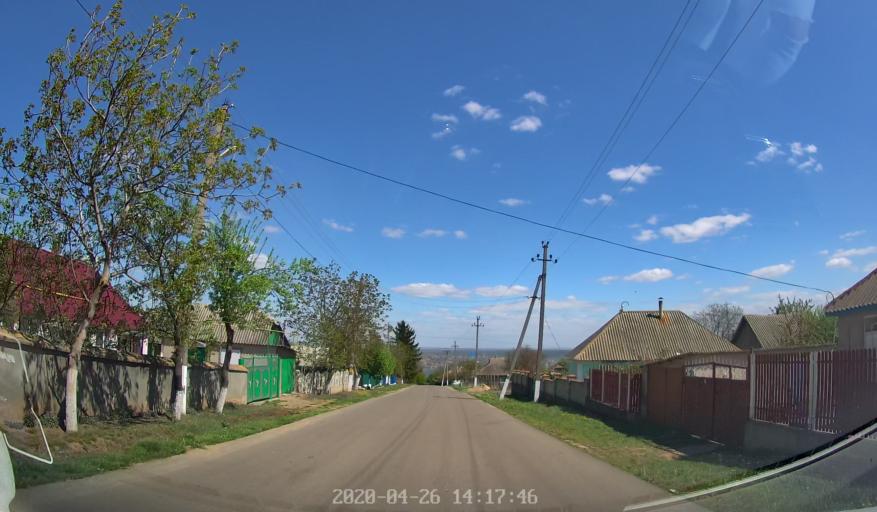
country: MD
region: Telenesti
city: Cocieri
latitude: 47.3540
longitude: 29.0537
